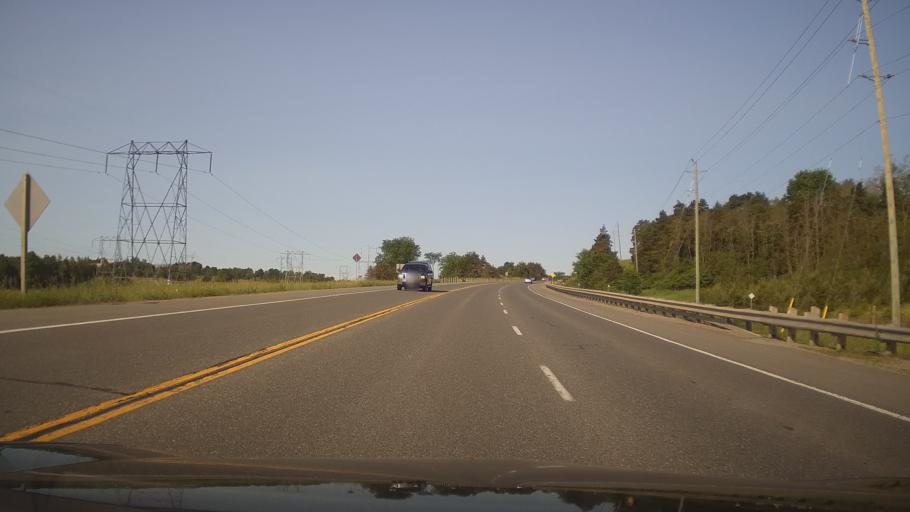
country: CA
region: Ontario
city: Peterborough
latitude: 44.3422
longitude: -78.0900
